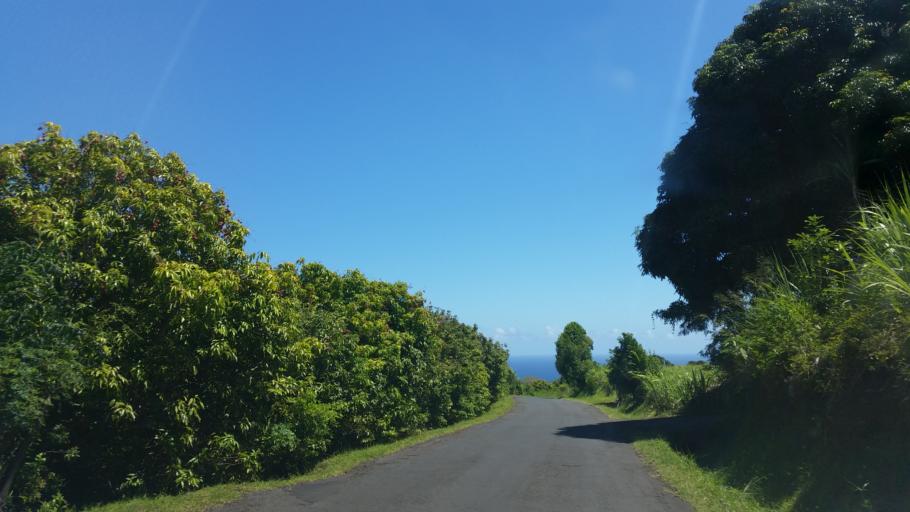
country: RE
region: Reunion
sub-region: Reunion
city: Sainte-Marie
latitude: -20.9338
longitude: 55.5287
